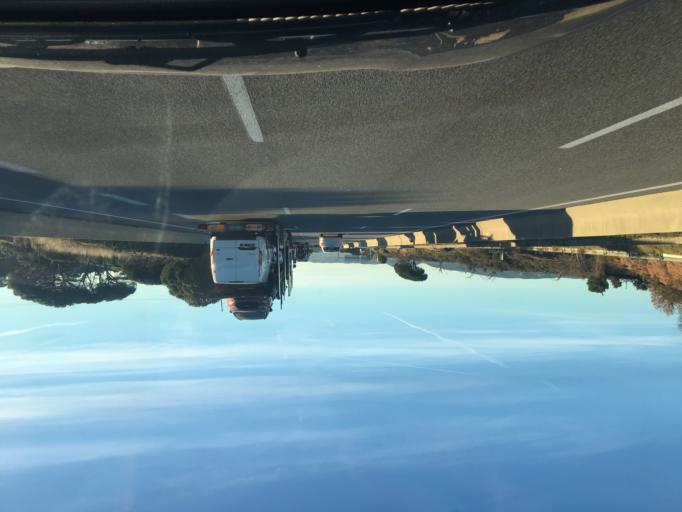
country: FR
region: Provence-Alpes-Cote d'Azur
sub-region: Departement du Var
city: Le Muy
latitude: 43.4592
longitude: 6.5545
